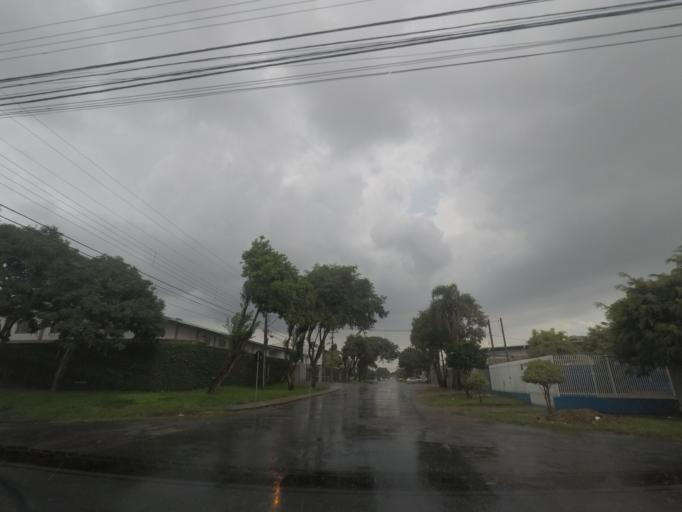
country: BR
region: Parana
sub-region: Curitiba
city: Curitiba
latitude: -25.4734
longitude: -49.2458
